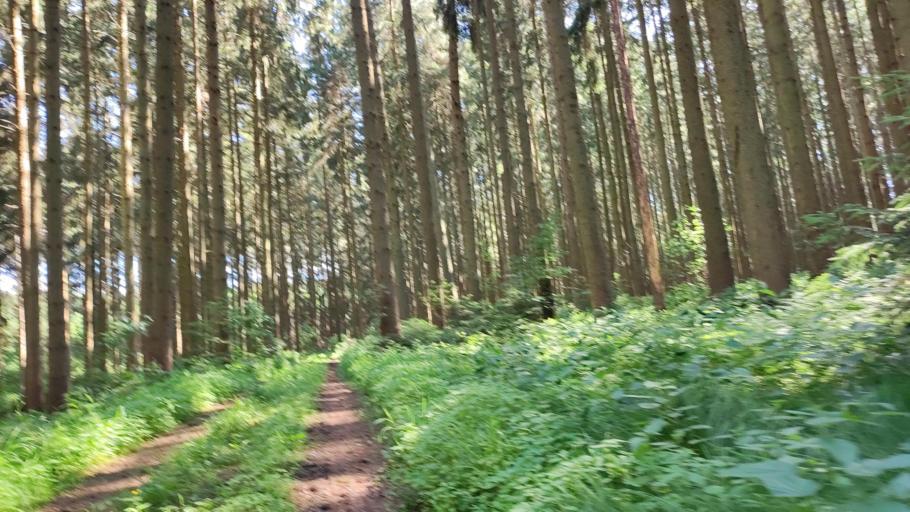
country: DE
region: Bavaria
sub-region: Swabia
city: Dinkelscherben
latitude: 48.3705
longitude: 10.6013
